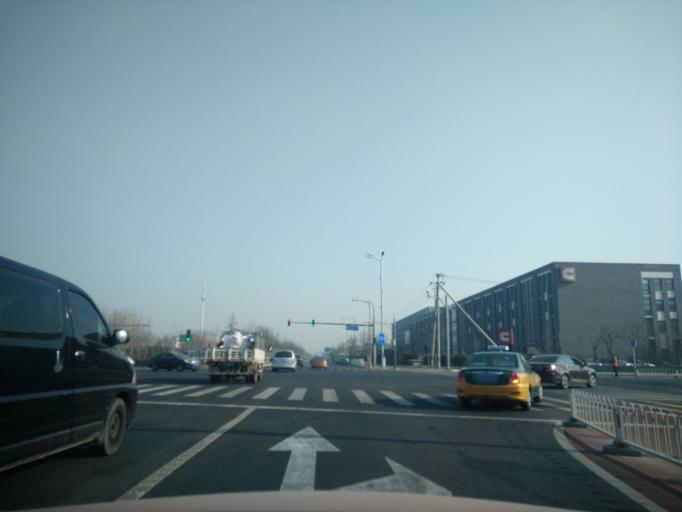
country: CN
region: Beijing
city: Jiugong
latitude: 39.7825
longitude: 116.5205
